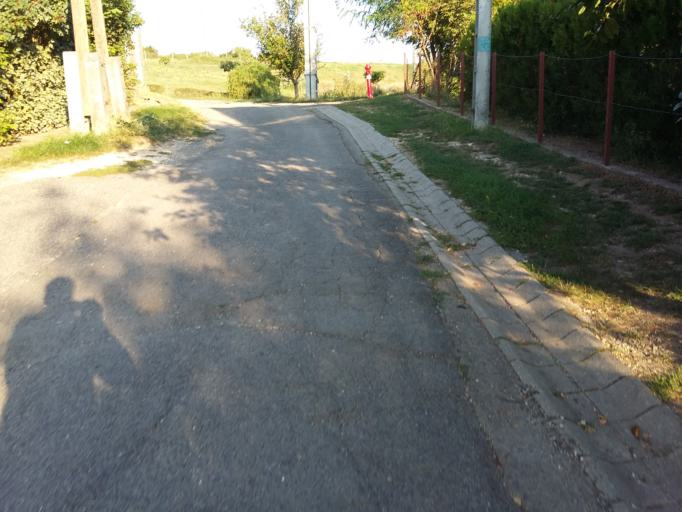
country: HU
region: Borsod-Abauj-Zemplen
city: Bekecs
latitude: 48.1589
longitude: 21.1786
